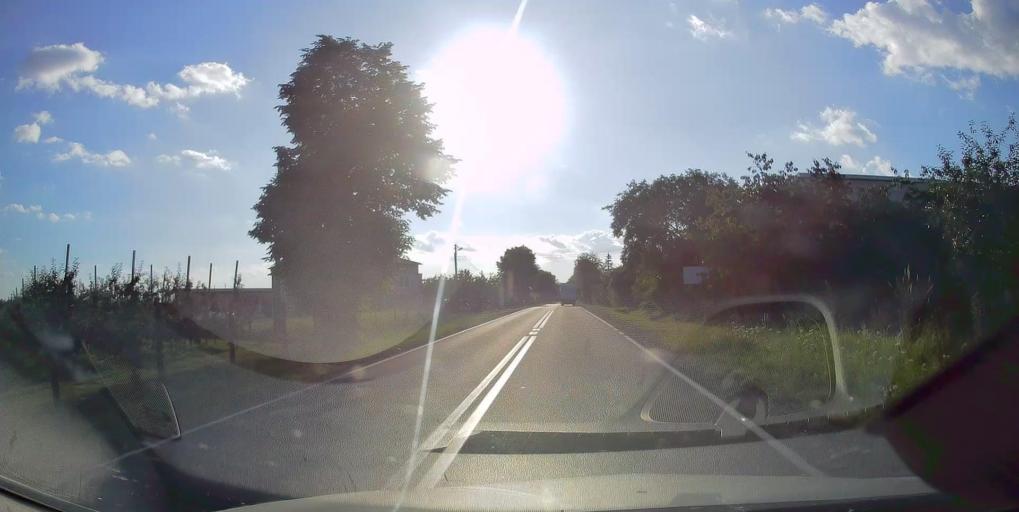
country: PL
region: Masovian Voivodeship
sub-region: Powiat grojecki
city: Bledow
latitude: 51.8022
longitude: 20.6071
